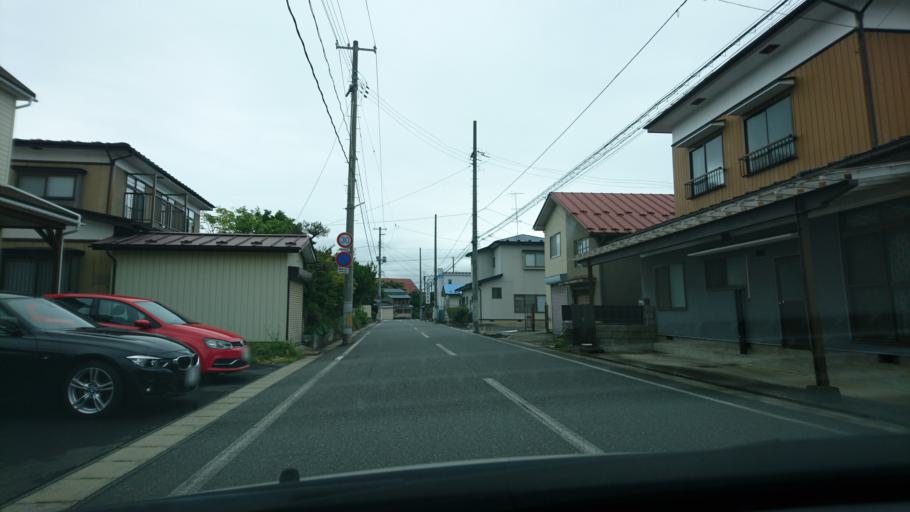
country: JP
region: Iwate
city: Ichinoseki
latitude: 38.9342
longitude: 141.1371
